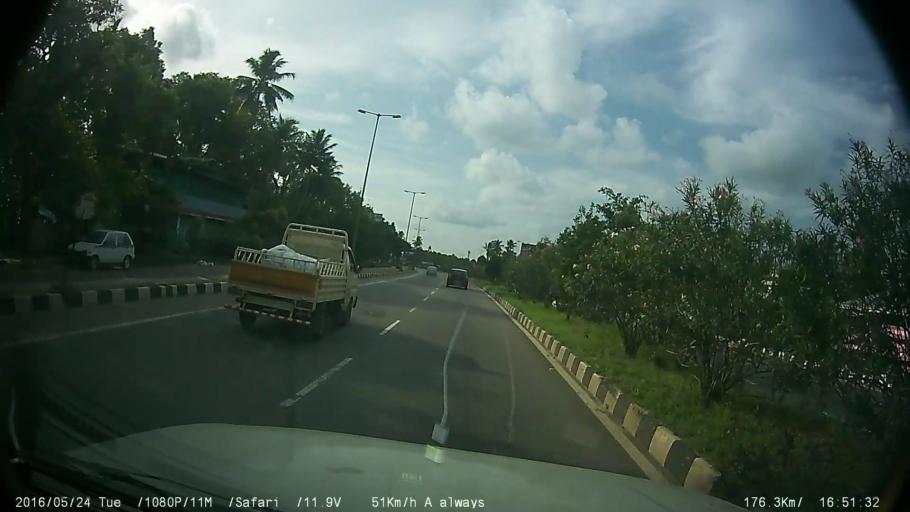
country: IN
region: Kerala
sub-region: Thrissur District
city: Kizhake Chalakudi
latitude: 10.3536
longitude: 76.3175
